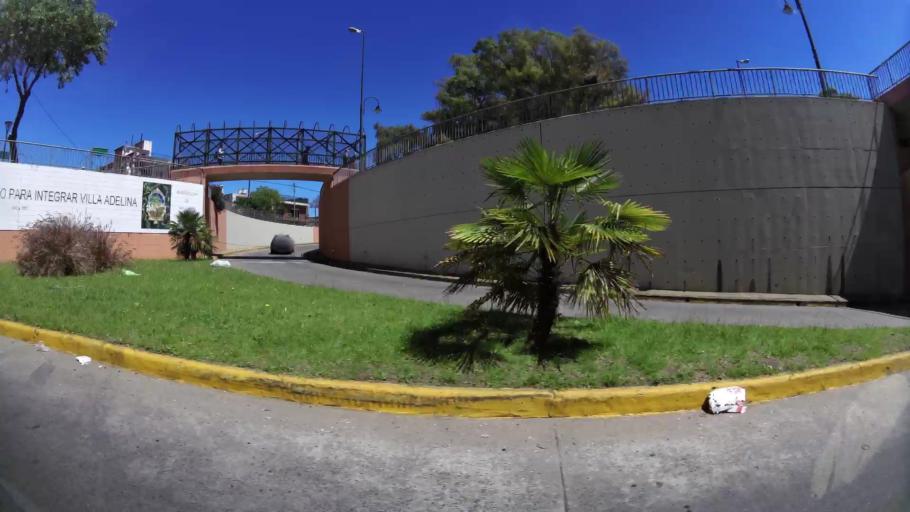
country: AR
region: Buenos Aires
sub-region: Partido de General San Martin
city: General San Martin
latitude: -34.5239
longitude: -58.5465
